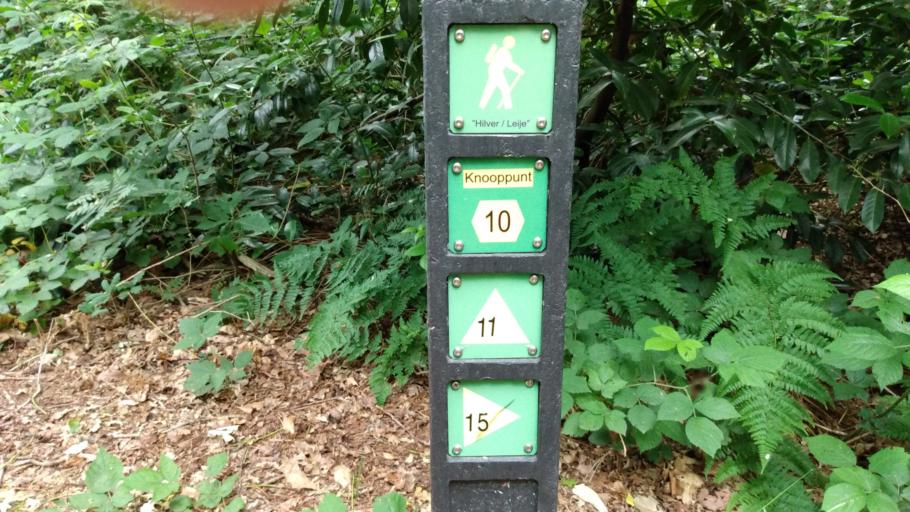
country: NL
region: North Brabant
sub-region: Gemeente Oisterwijk
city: Oisterwijk
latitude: 51.5469
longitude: 5.1604
